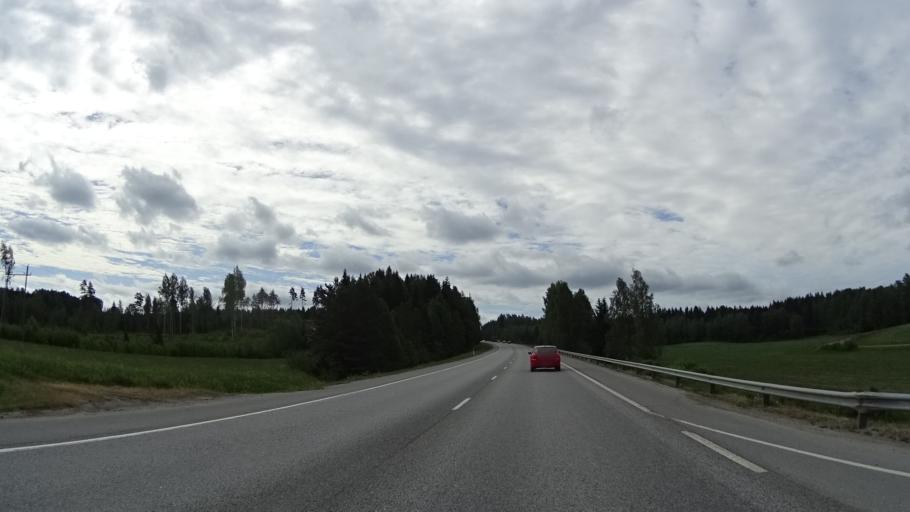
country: FI
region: Uusimaa
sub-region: Helsinki
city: Vihti
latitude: 60.3660
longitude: 24.3190
